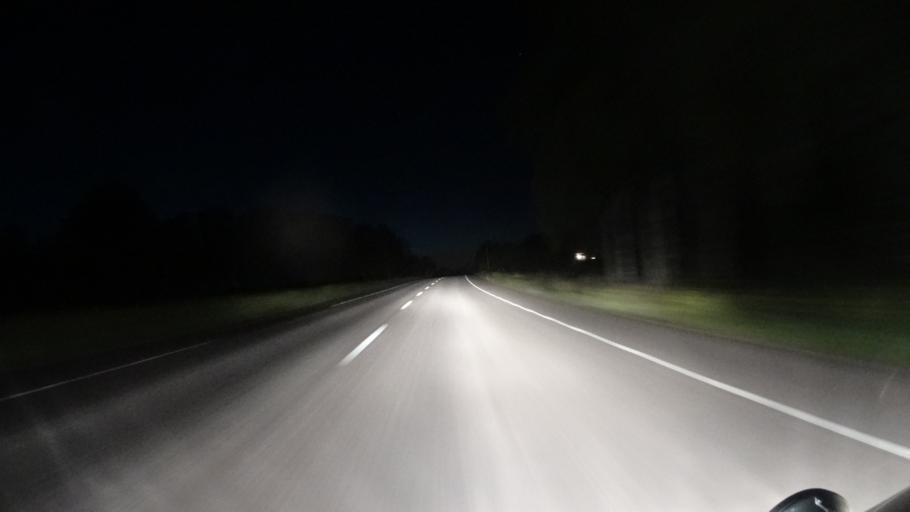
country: SE
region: OEstergoetland
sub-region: Odeshogs Kommun
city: OEdeshoeg
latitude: 58.2708
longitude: 14.7517
